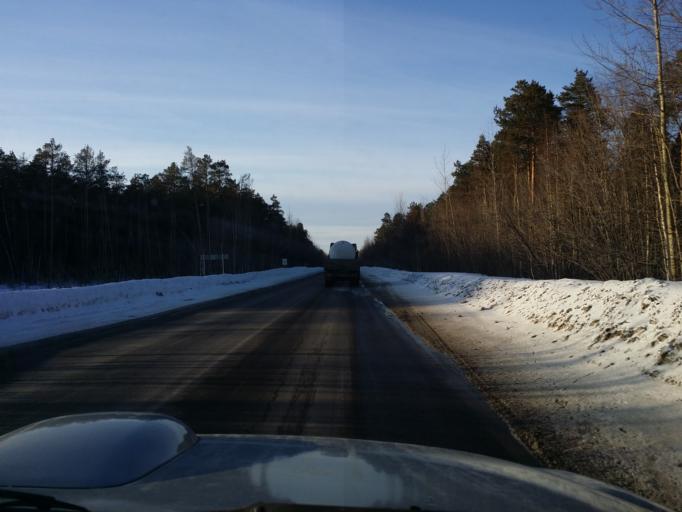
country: RU
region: Khanty-Mansiyskiy Avtonomnyy Okrug
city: Izluchinsk
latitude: 60.9443
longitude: 76.8557
